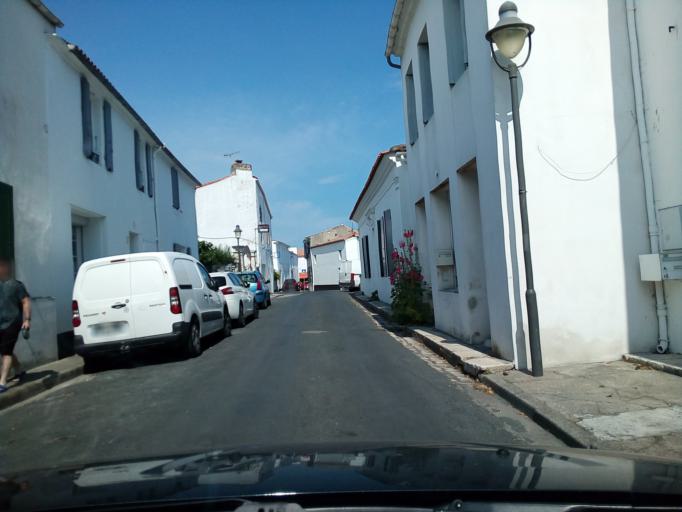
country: FR
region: Poitou-Charentes
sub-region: Departement de la Charente-Maritime
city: Dolus-d'Oleron
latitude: 45.9440
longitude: -1.3040
